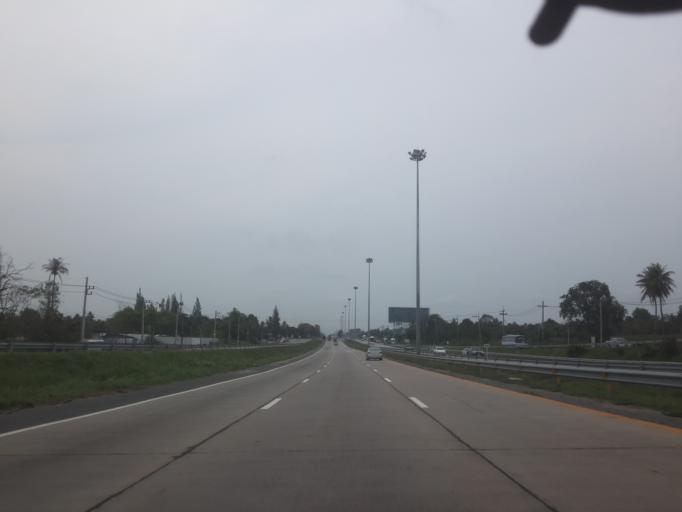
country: TH
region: Chon Buri
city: Bang Lamung
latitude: 12.9686
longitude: 100.9812
